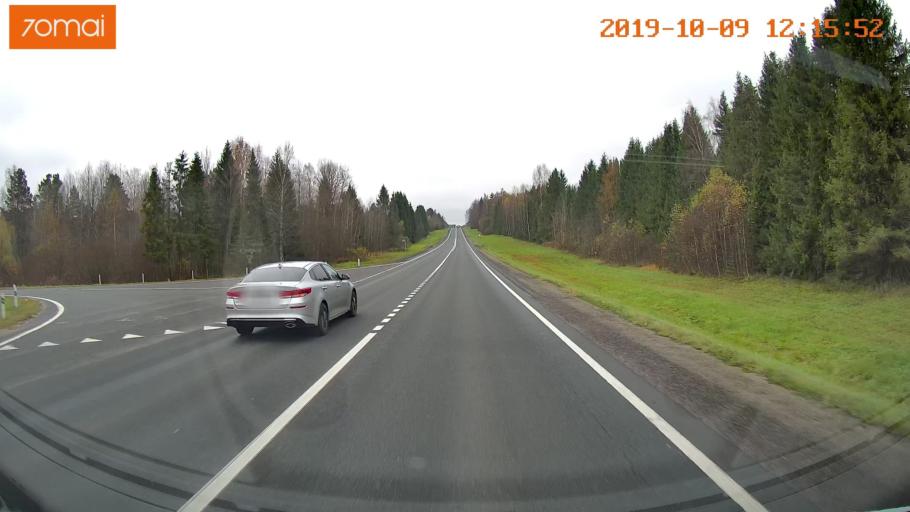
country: RU
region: Jaroslavl
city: Prechistoye
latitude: 58.4770
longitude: 40.3222
